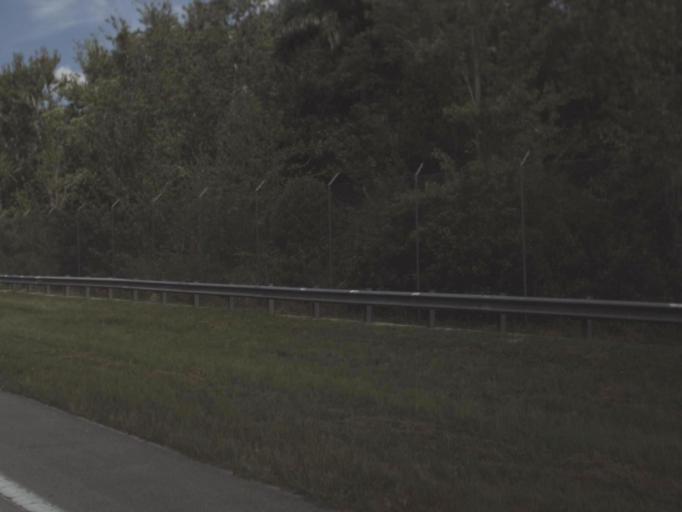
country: US
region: Florida
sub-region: Collier County
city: Orangetree
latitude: 26.0551
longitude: -81.3445
